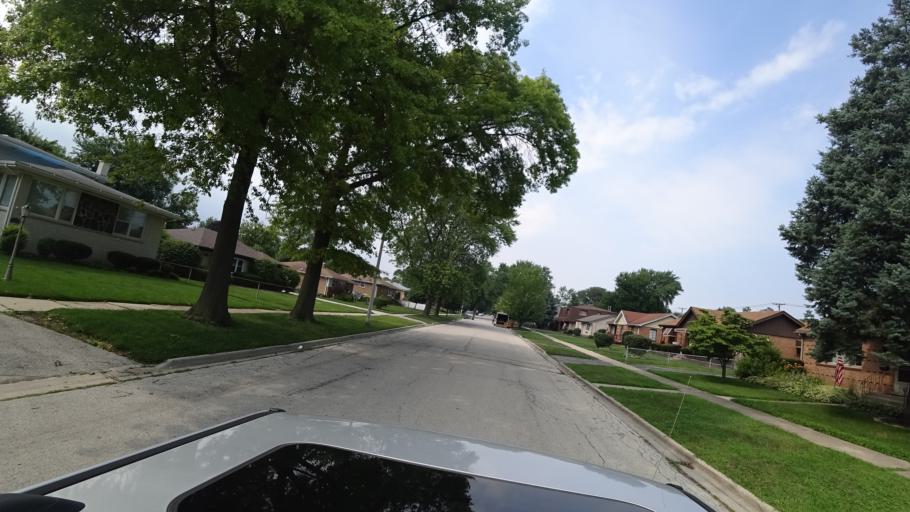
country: US
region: Illinois
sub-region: Cook County
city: Chicago Ridge
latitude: 41.6926
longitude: -87.7765
